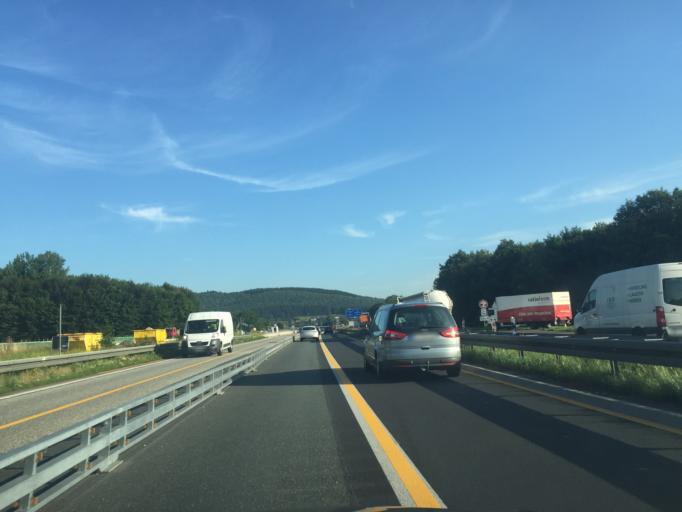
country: DE
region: North Rhine-Westphalia
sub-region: Regierungsbezirk Arnsberg
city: Wenden
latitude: 50.9870
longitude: 7.8368
